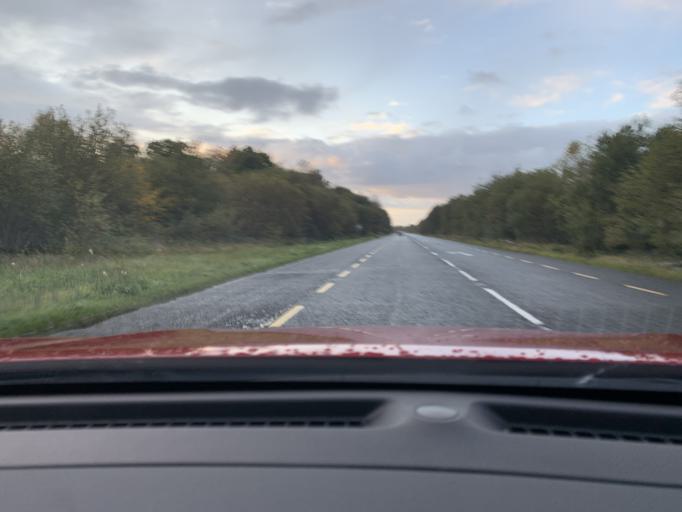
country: IE
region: Connaught
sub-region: County Leitrim
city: Carrick-on-Shannon
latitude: 53.9519
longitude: -8.1522
